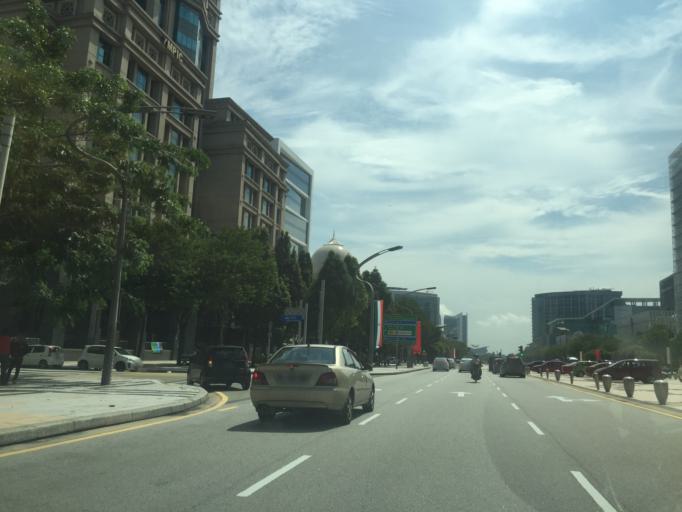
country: MY
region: Putrajaya
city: Putrajaya
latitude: 2.9208
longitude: 101.6863
